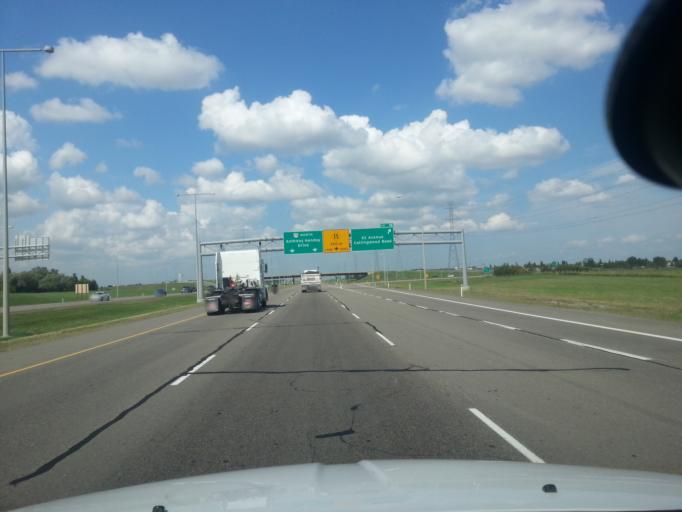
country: CA
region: Alberta
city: Devon
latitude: 53.4889
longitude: -113.6592
